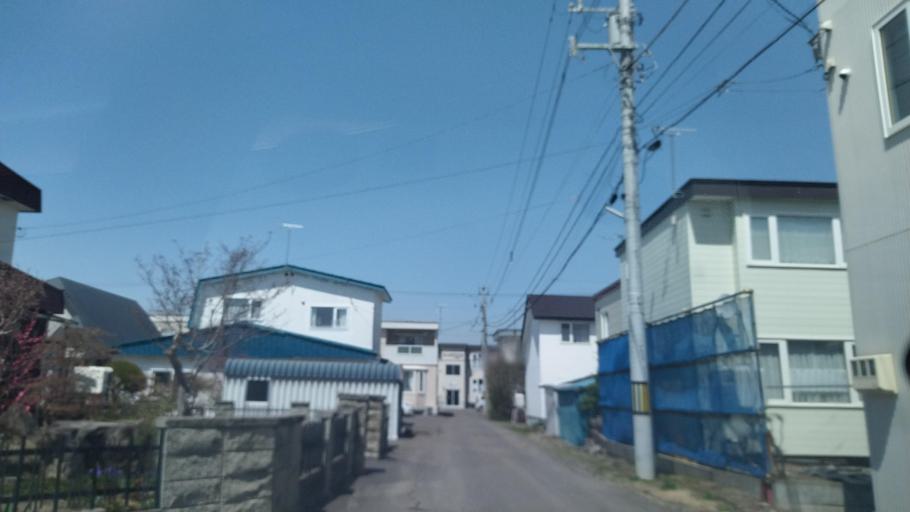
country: JP
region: Hokkaido
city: Obihiro
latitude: 42.9318
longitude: 143.1740
